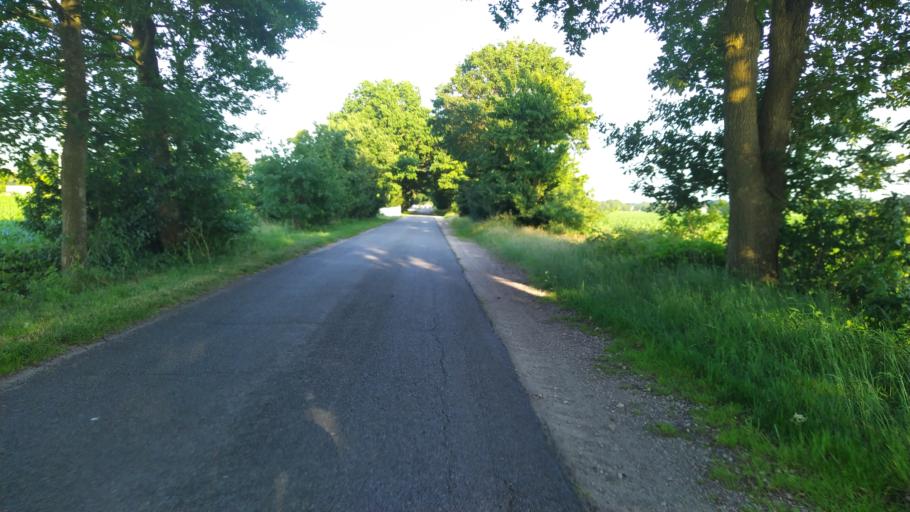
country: DE
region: Lower Saxony
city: Alfstedt
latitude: 53.5535
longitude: 9.0504
